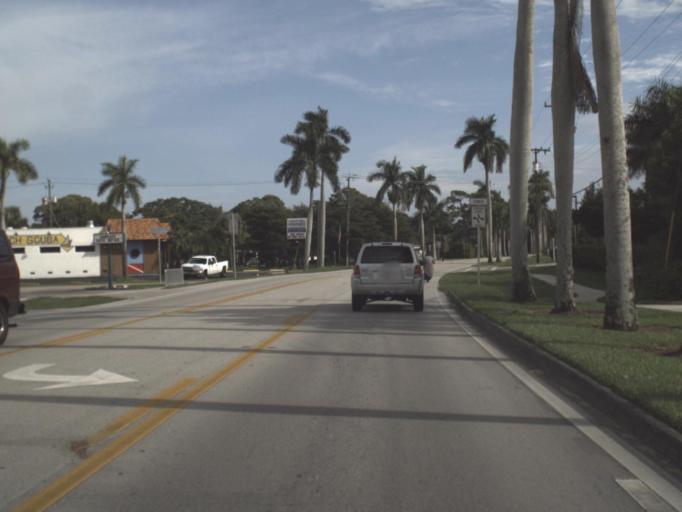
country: US
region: Florida
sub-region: Lee County
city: McGregor
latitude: 26.5592
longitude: -81.9096
